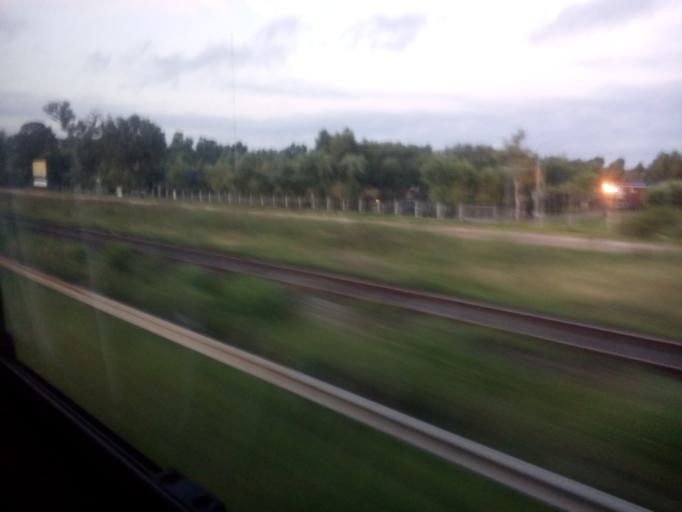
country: AR
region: Buenos Aires
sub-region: Partido de Zarate
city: Zarate
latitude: -34.0485
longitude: -58.9871
